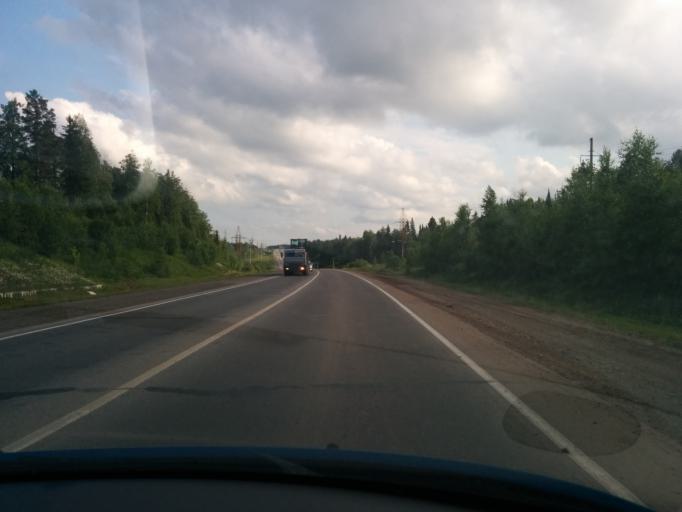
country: RU
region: Perm
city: Novyye Lyady
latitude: 58.0616
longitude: 56.4270
